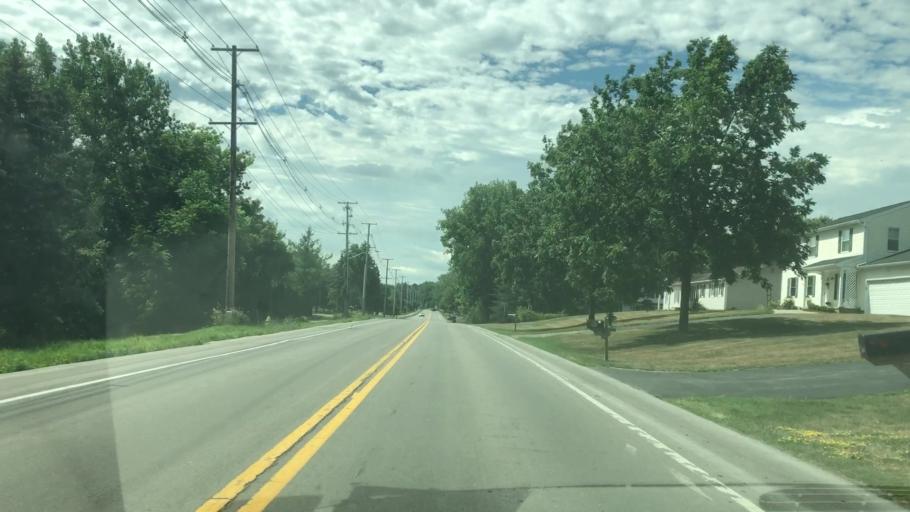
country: US
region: New York
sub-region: Monroe County
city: Fairport
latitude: 43.0847
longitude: -77.4023
